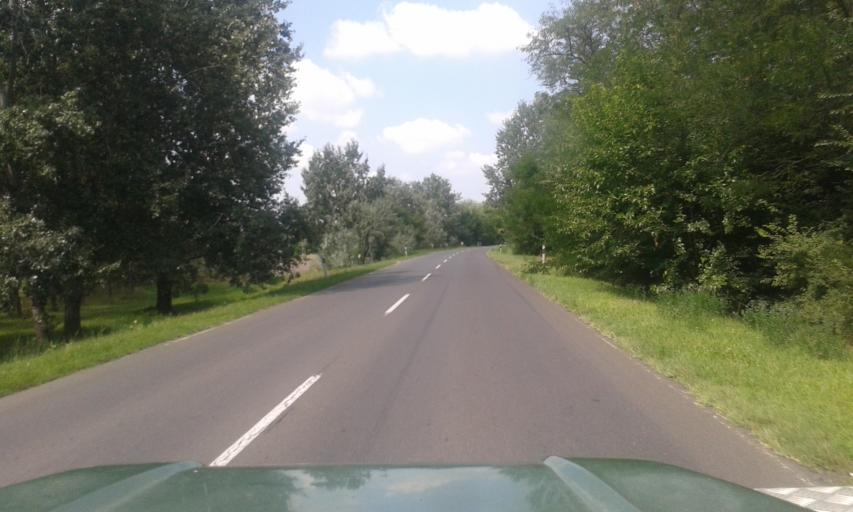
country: HU
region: Csongrad
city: Szatymaz
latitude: 46.3615
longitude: 20.0486
